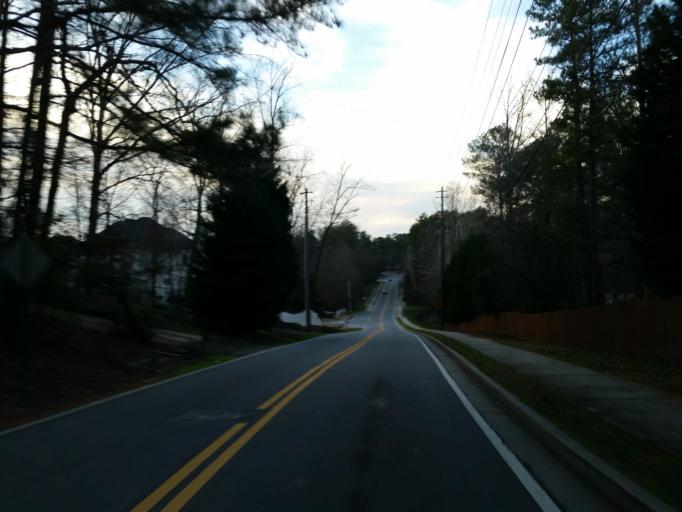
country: US
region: Georgia
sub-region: Cobb County
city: Marietta
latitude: 33.9836
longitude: -84.5073
